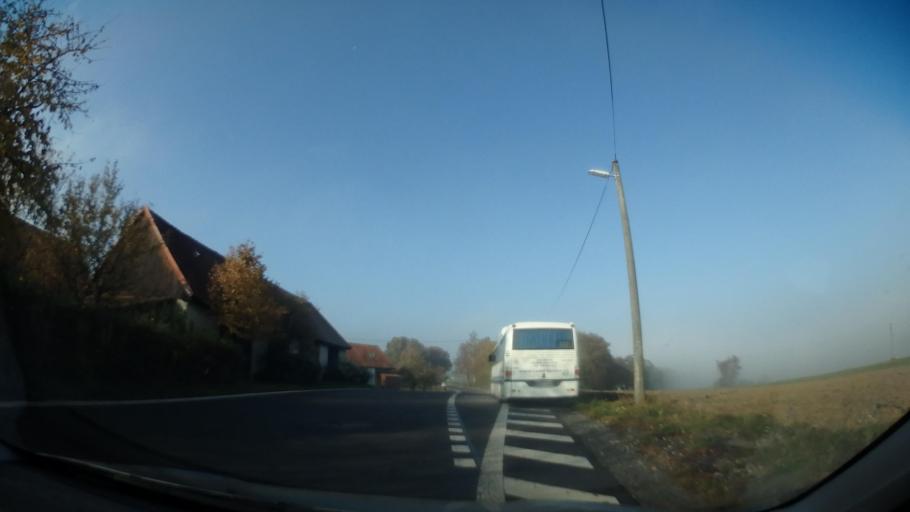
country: CZ
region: Vysocina
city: Krizanov
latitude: 49.4397
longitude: 16.1737
